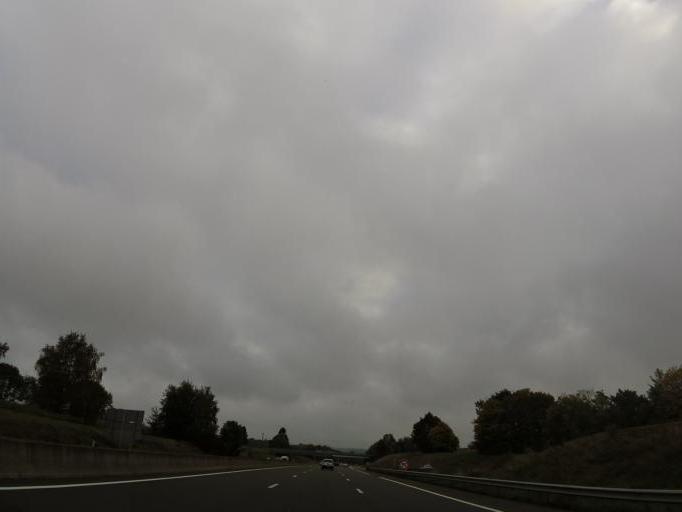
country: FR
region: Ile-de-France
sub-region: Departement de Seine-et-Marne
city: Saint-Germain-sur-Morin
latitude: 48.8609
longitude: 2.8449
